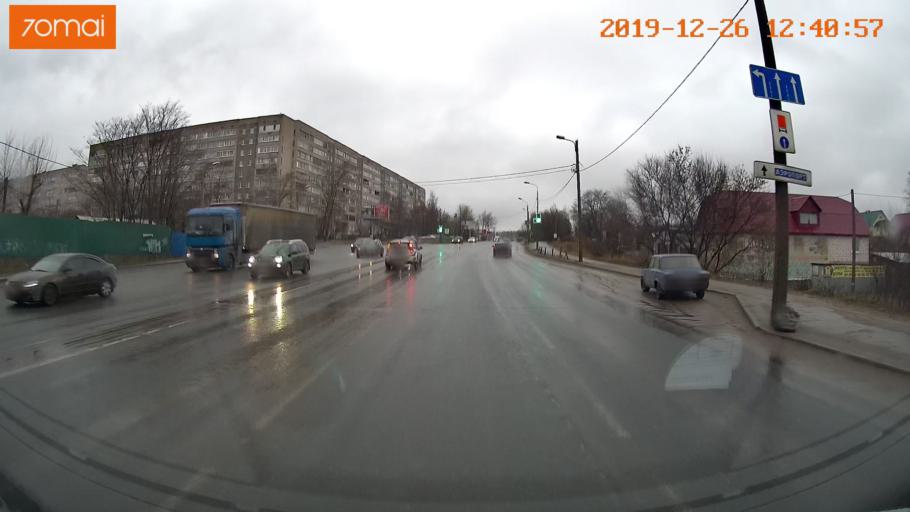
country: RU
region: Vologda
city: Tonshalovo
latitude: 59.1455
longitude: 37.9669
